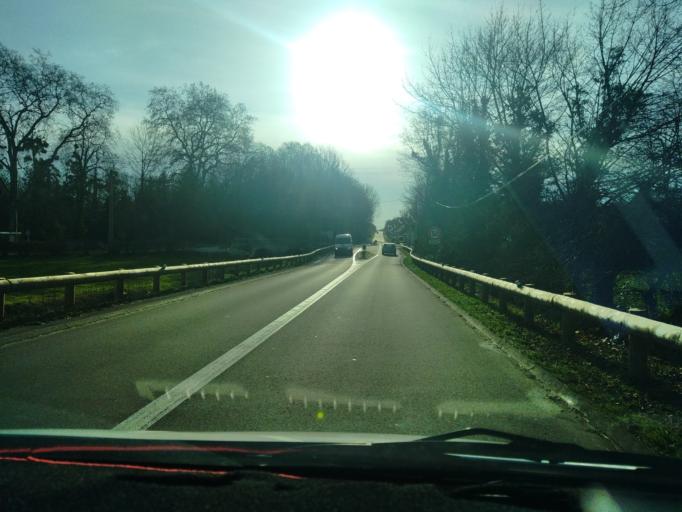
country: FR
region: Franche-Comte
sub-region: Departement de la Haute-Saone
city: Gray
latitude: 47.3916
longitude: 5.6521
